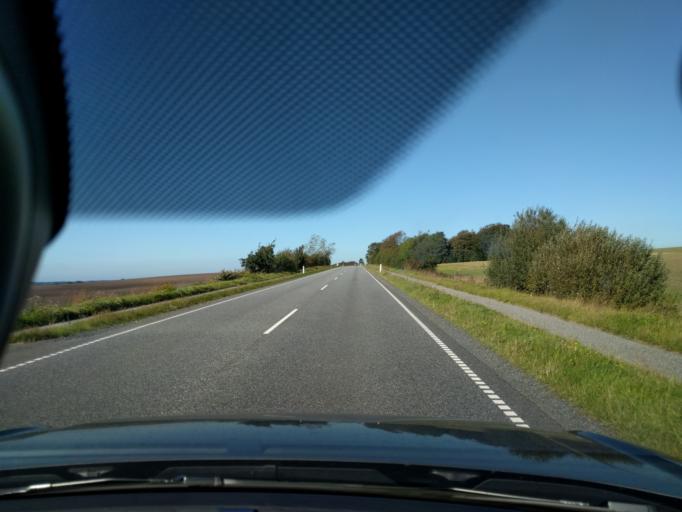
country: DK
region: North Denmark
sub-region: Vesthimmerland Kommune
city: Aars
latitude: 56.7366
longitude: 9.6008
